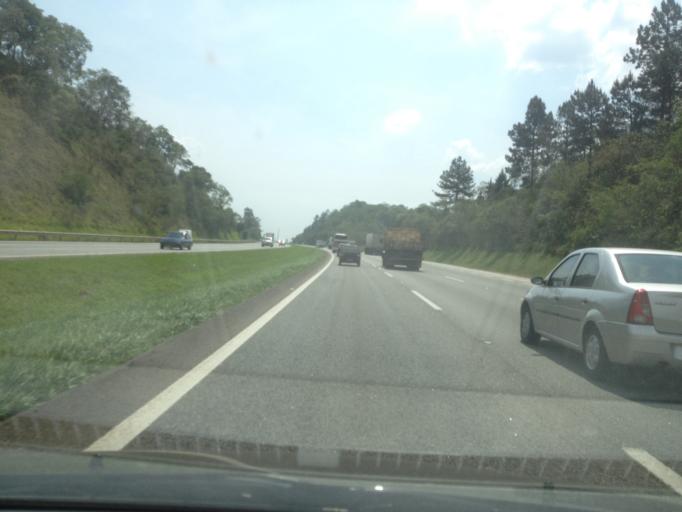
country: BR
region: Sao Paulo
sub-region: Pirapora Do Bom Jesus
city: Pirapora do Bom Jesus
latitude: -23.4721
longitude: -47.0078
